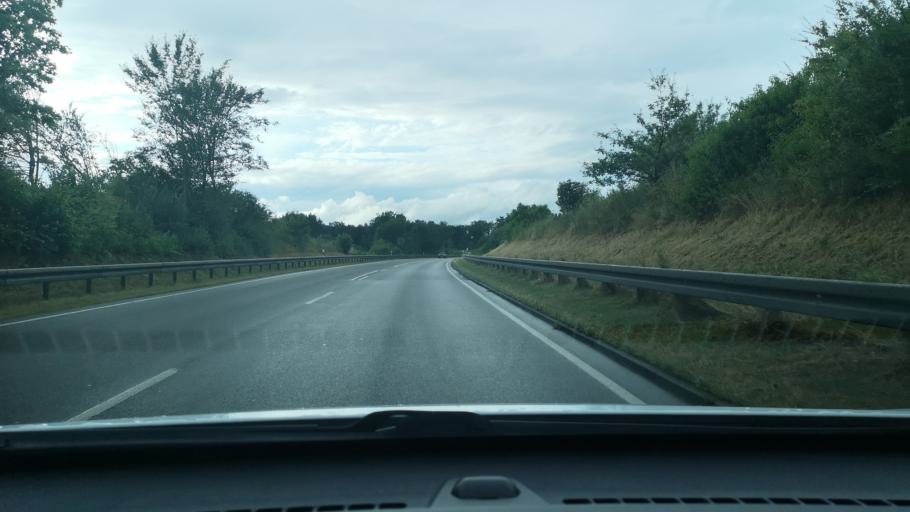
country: DE
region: Baden-Wuerttemberg
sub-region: Freiburg Region
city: Zimmern ob Rottweil
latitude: 48.1545
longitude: 8.6041
